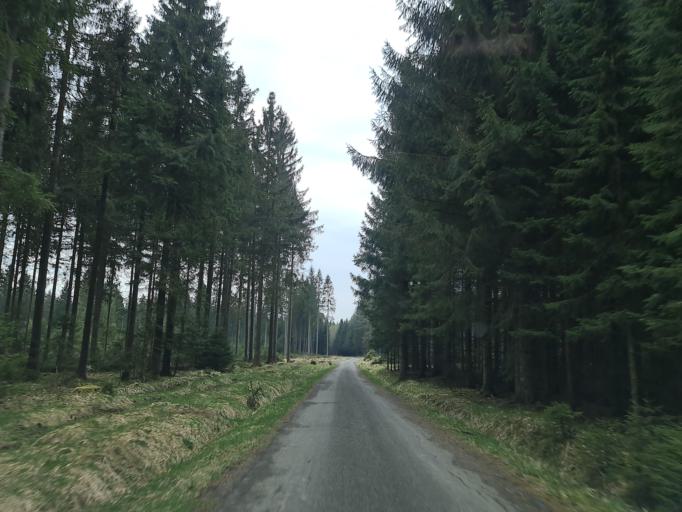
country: DE
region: Saxony
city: Grunbach
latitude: 50.4490
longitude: 12.3882
